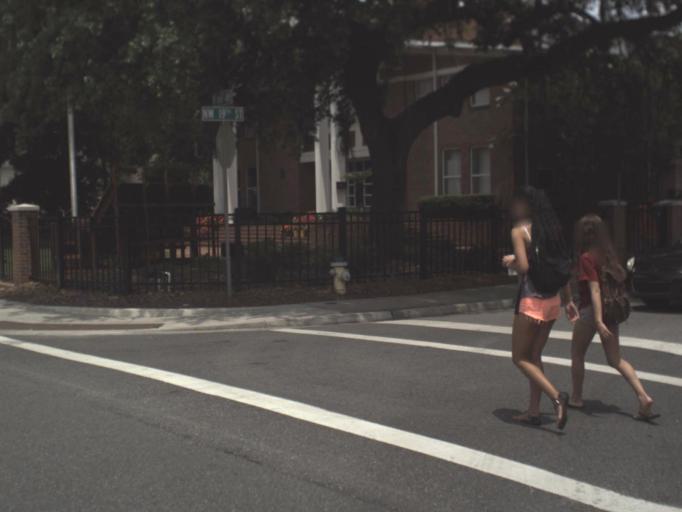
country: US
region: Florida
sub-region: Alachua County
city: Gainesville
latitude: 29.6521
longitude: -82.3477
